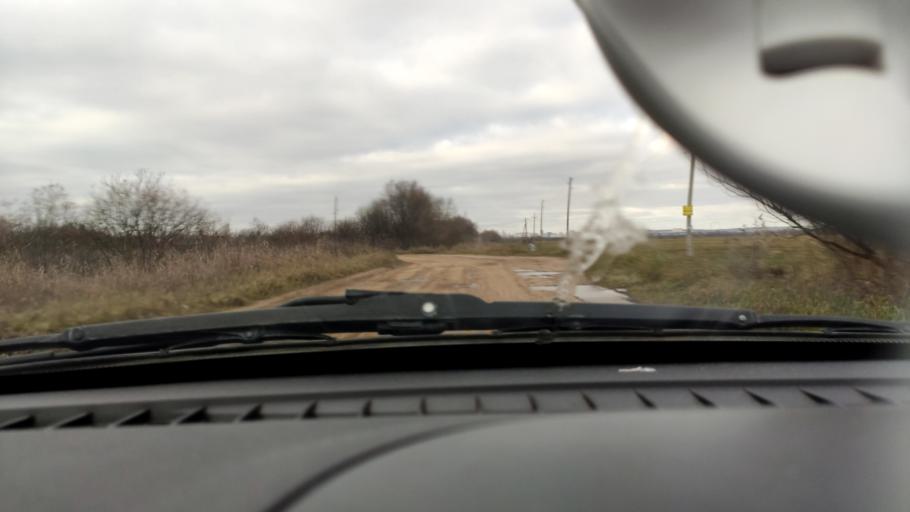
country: RU
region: Perm
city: Kondratovo
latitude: 57.9867
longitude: 56.0818
